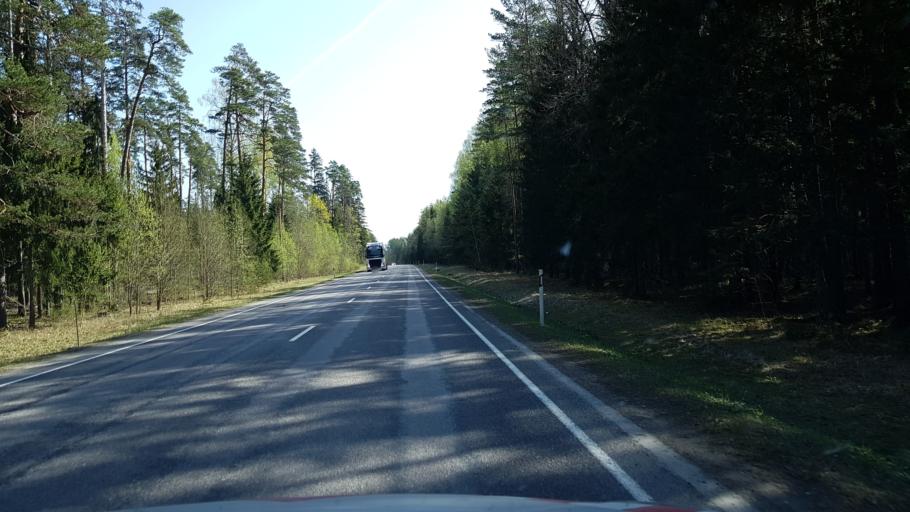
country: EE
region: Viljandimaa
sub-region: Moisakuela linn
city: Moisakula
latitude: 58.2467
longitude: 25.1513
